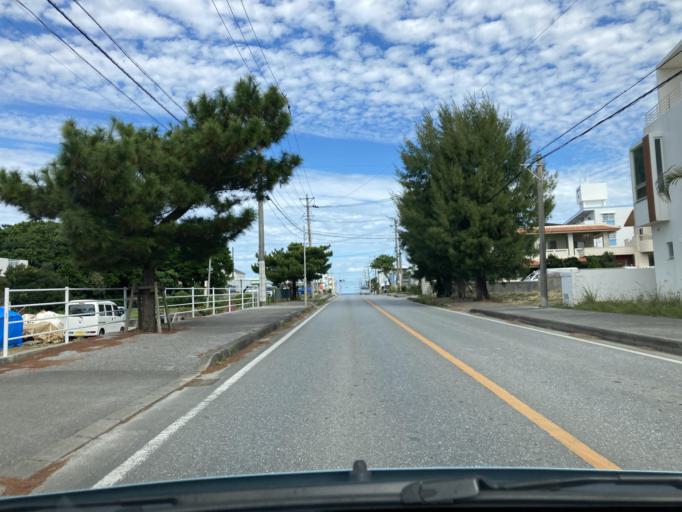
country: JP
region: Okinawa
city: Ishikawa
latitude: 26.4147
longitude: 127.7324
